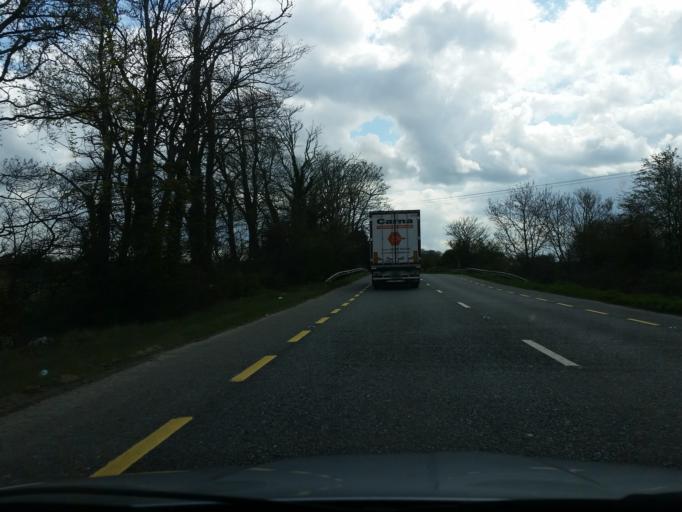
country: IE
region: Leinster
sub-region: An Mhi
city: Ashbourne
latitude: 53.5413
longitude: -6.4277
